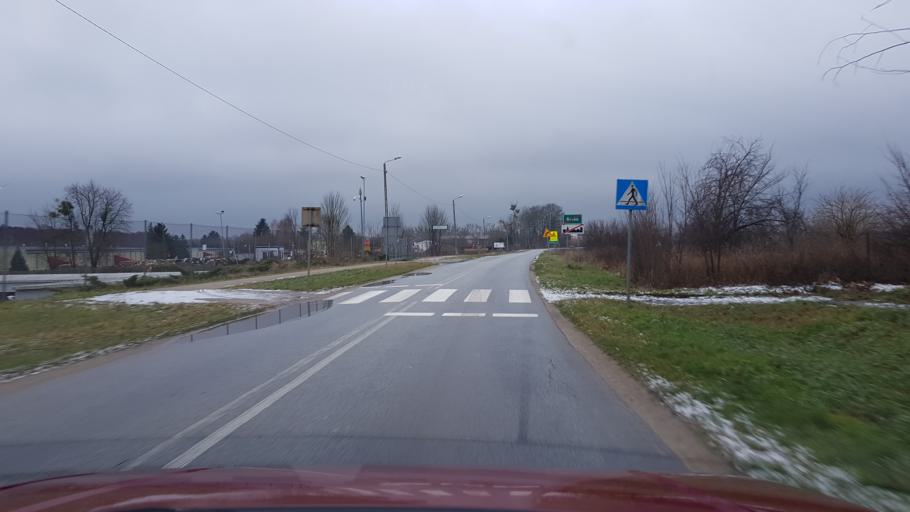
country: PL
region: West Pomeranian Voivodeship
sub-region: Powiat lobeski
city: Resko
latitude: 53.7658
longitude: 15.3990
